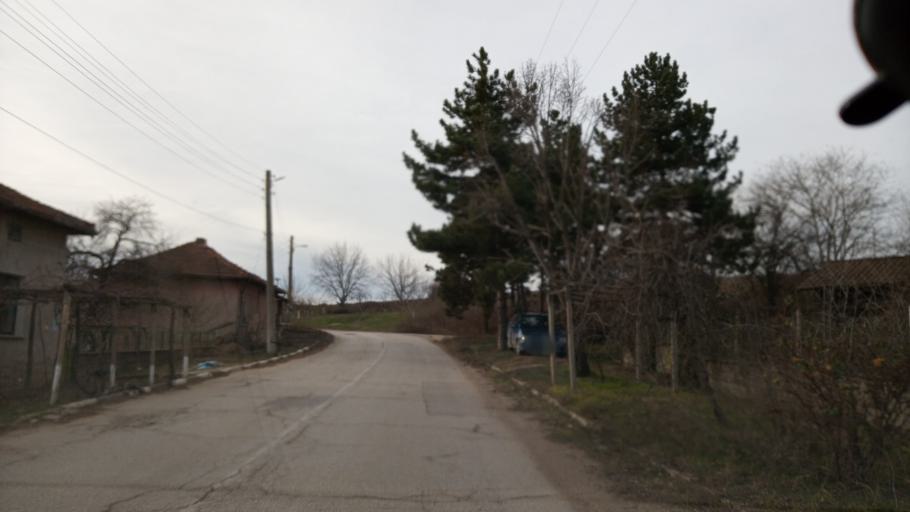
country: BG
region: Pleven
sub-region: Obshtina Belene
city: Belene
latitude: 43.6288
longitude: 25.0395
